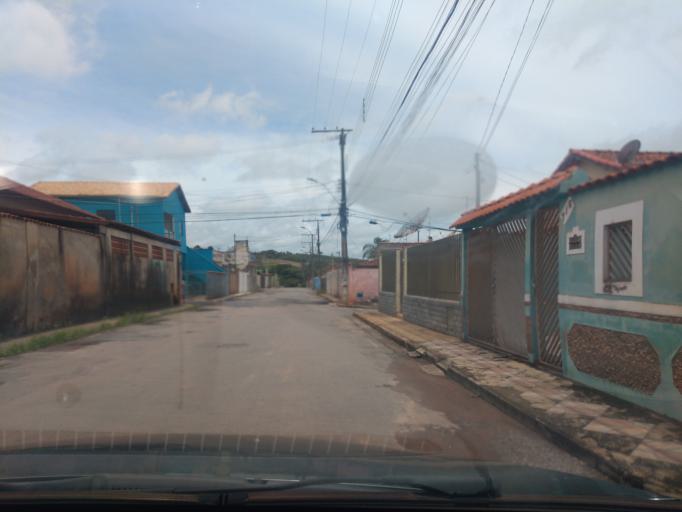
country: BR
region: Minas Gerais
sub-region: Tres Coracoes
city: Tres Coracoes
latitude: -21.6813
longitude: -45.2594
